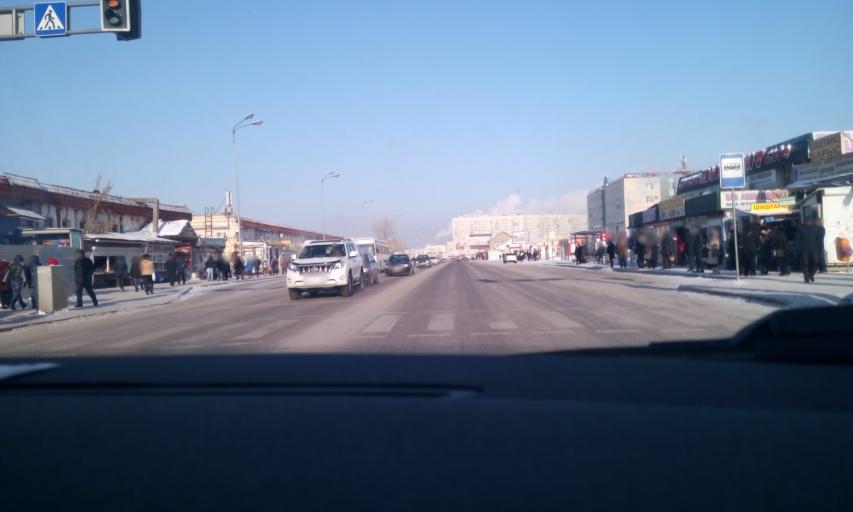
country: KZ
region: Astana Qalasy
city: Astana
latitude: 51.1746
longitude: 71.4377
